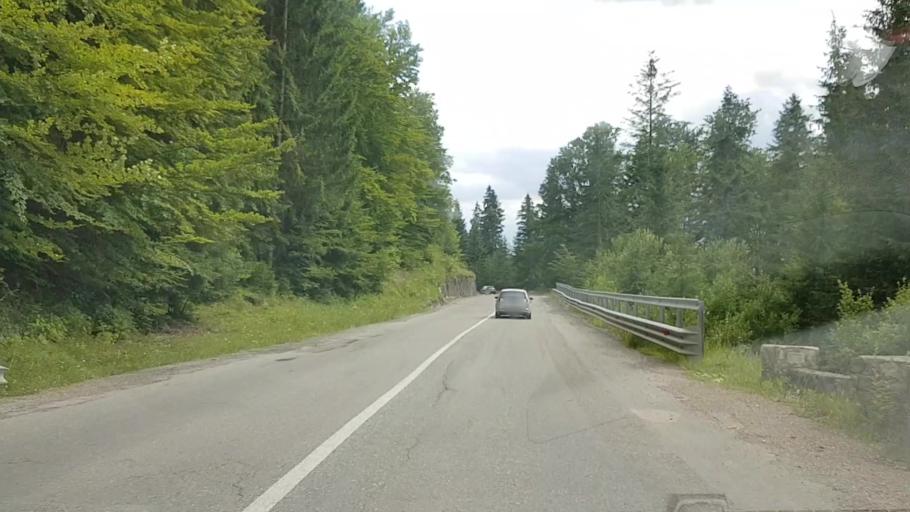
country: RO
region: Neamt
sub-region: Comuna Pangarati
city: Pangarati
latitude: 46.9748
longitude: 26.1170
